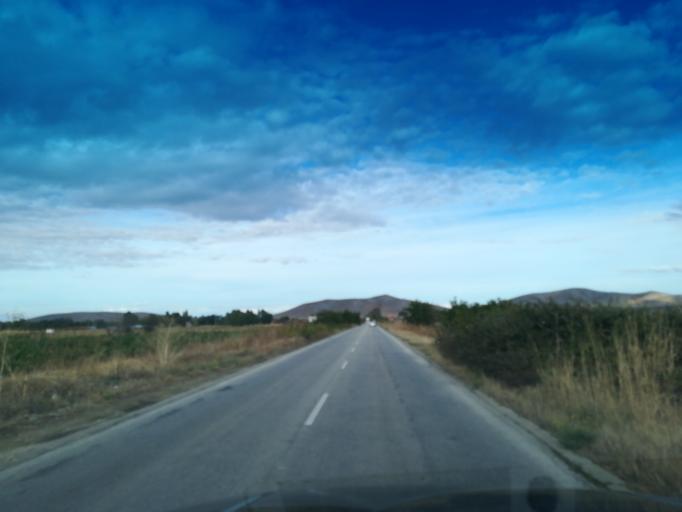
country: BG
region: Plovdiv
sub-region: Obshtina Krichim
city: Krichim
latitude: 42.0786
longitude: 24.4165
